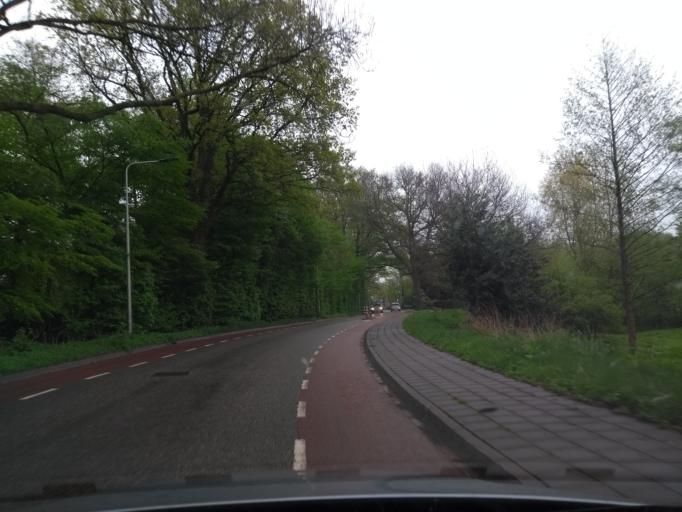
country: DE
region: Lower Saxony
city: Getelo
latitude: 52.4141
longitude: 6.9026
